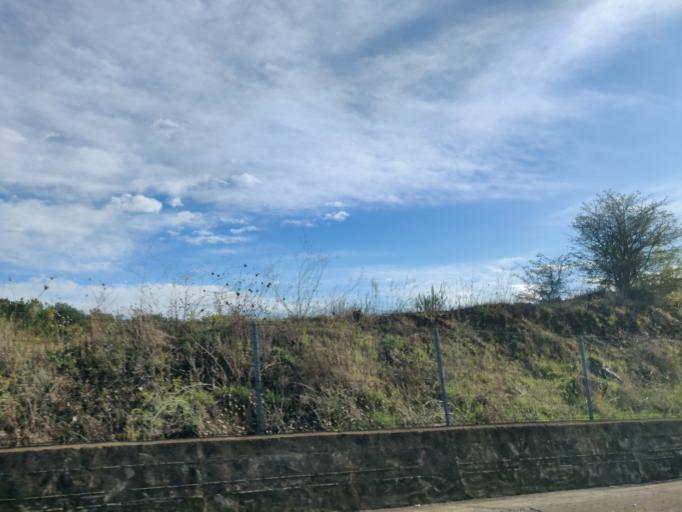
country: IT
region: Tuscany
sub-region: Provincia di Grosseto
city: Ribolla
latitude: 42.9204
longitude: 11.0032
